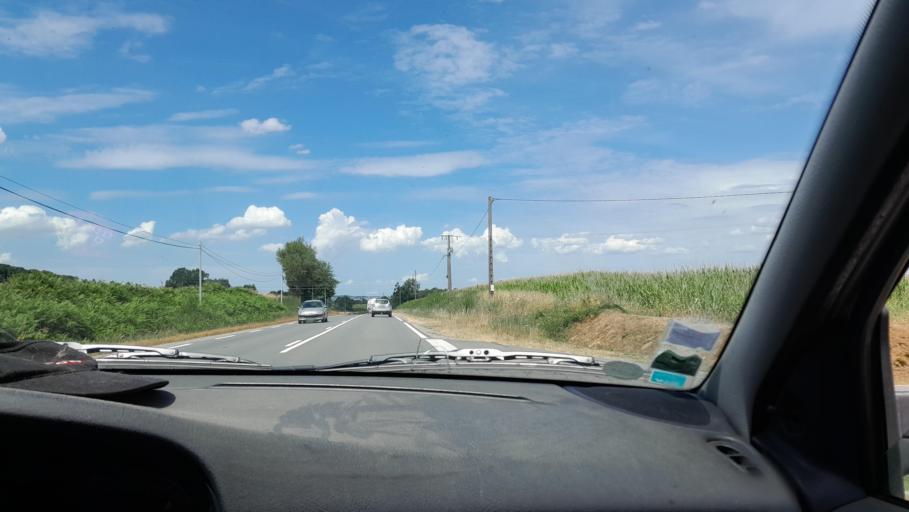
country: FR
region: Brittany
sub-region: Departement d'Ille-et-Vilaine
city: Luitre
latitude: 48.2913
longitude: -1.1568
